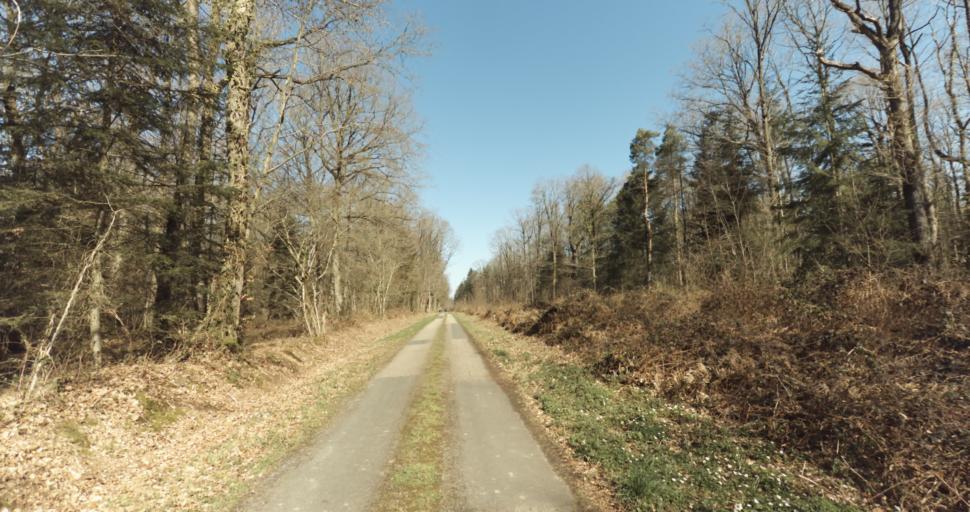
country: FR
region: Lower Normandy
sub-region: Departement du Calvados
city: Livarot
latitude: 48.9717
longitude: 0.0730
